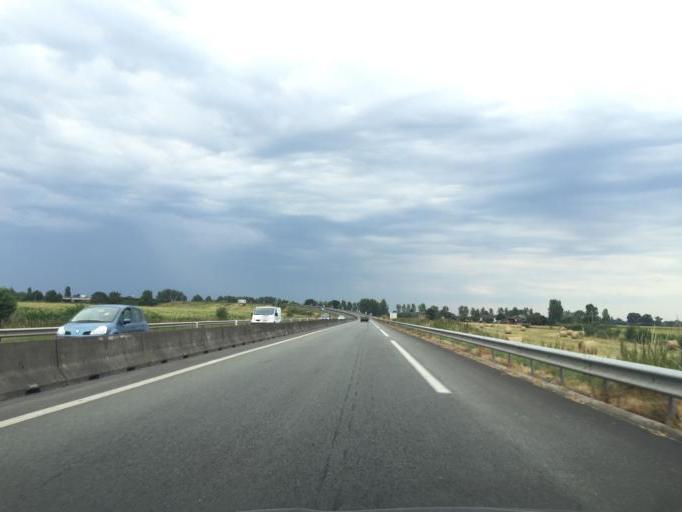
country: FR
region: Auvergne
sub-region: Departement de l'Allier
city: Toulon-sur-Allier
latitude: 46.5061
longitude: 3.3567
